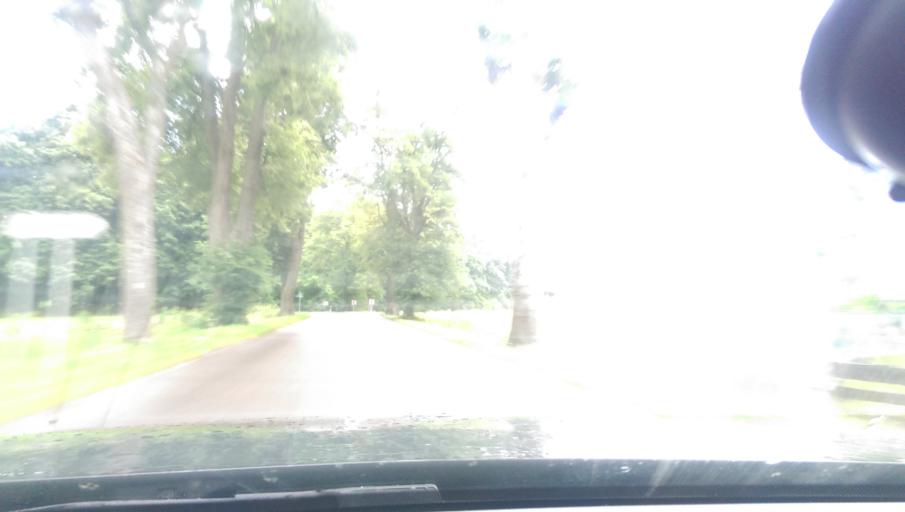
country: PL
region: Warmian-Masurian Voivodeship
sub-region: Powiat piski
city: Ruciane-Nida
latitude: 53.6910
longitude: 21.4821
